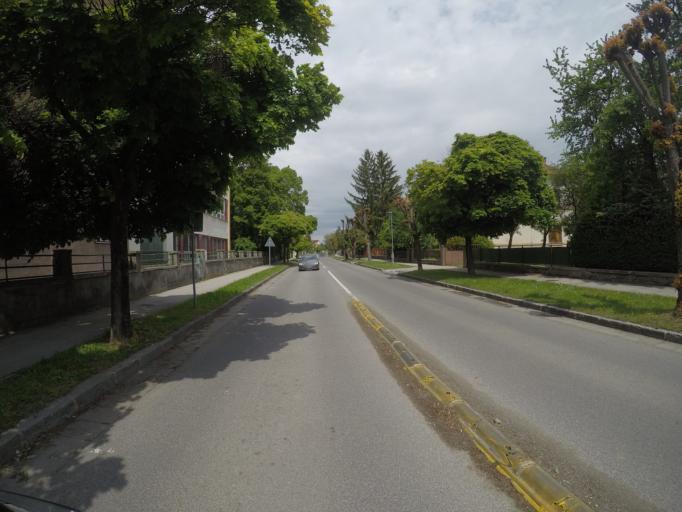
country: SK
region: Banskobystricky
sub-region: Okres Banska Bystrica
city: Zvolen
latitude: 48.5744
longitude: 19.1216
